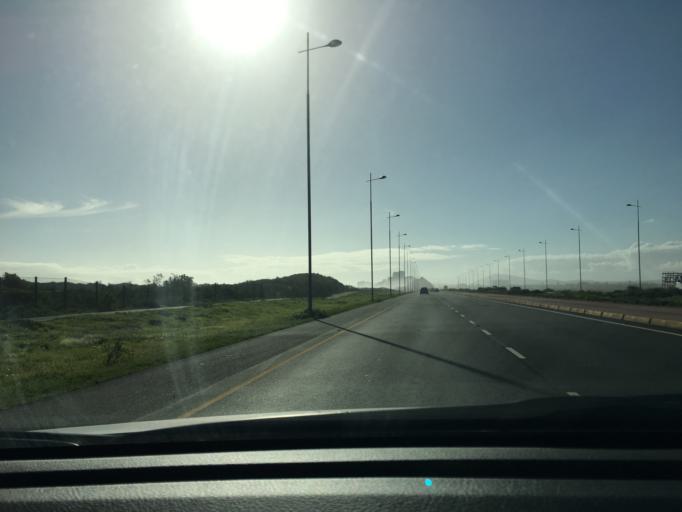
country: ZA
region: Western Cape
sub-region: City of Cape Town
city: Sunset Beach
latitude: -33.8408
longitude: 18.4864
